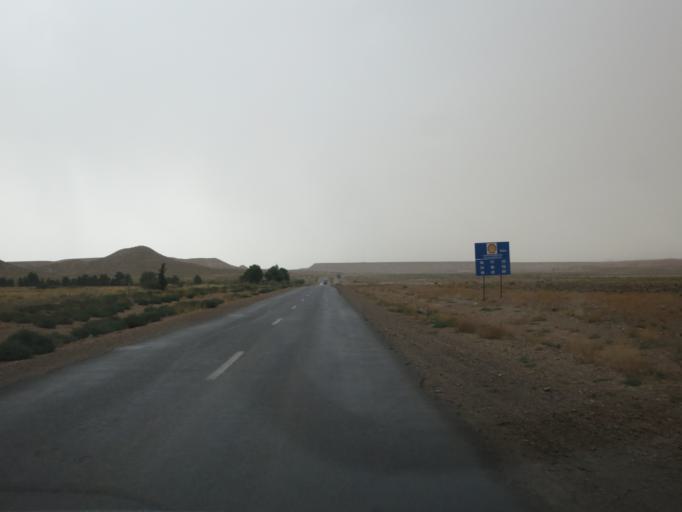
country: MA
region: Meknes-Tafilalet
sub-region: Khenifra
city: Midelt
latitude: 32.6795
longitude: -4.6727
